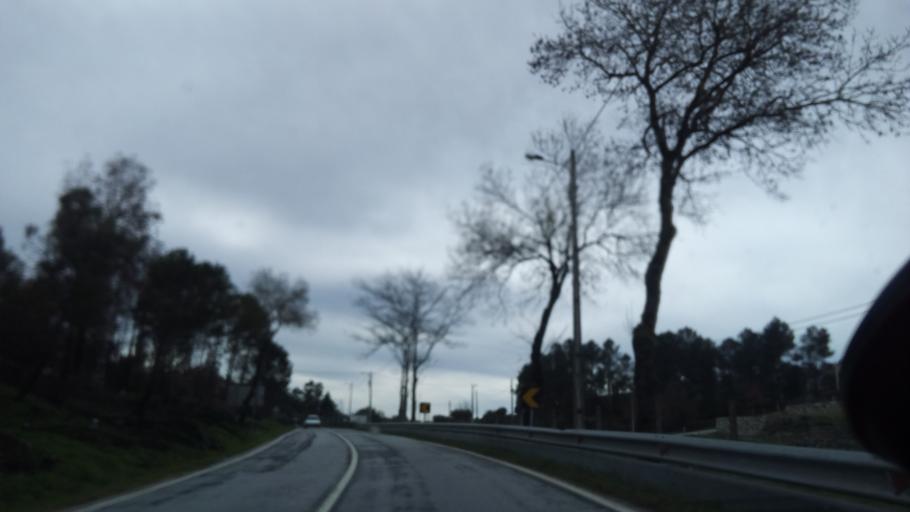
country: PT
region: Guarda
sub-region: Seia
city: Seia
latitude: 40.4854
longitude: -7.6625
